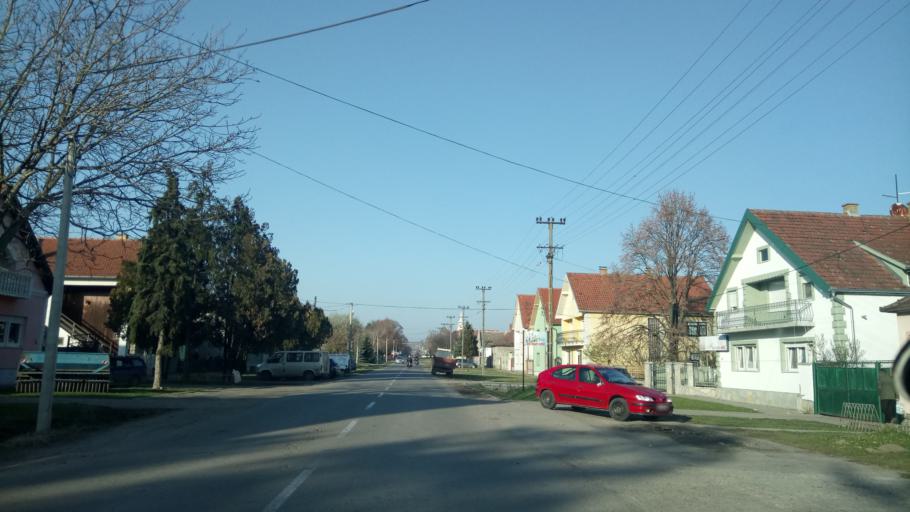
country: RS
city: Beska
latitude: 45.1260
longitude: 20.0674
